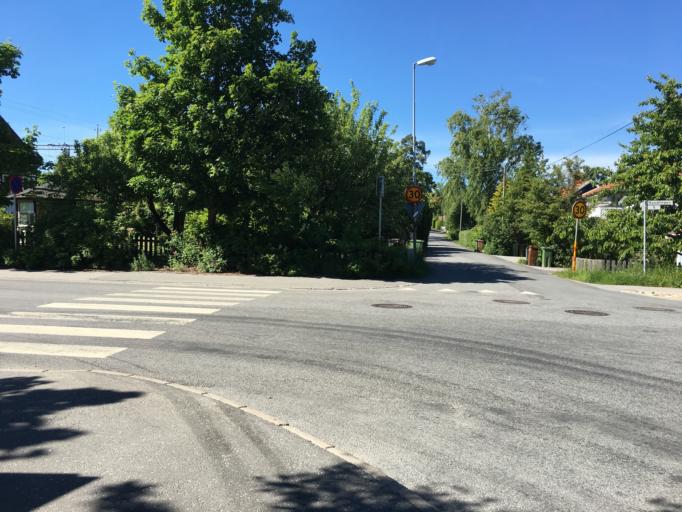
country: SE
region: Stockholm
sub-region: Sollentuna Kommun
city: Sollentuna
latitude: 59.4159
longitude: 17.9588
